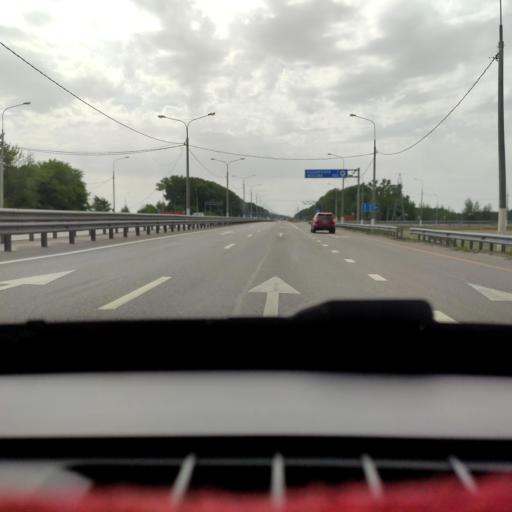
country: RU
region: Voronezj
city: Kashirskoye
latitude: 51.3936
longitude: 39.5696
